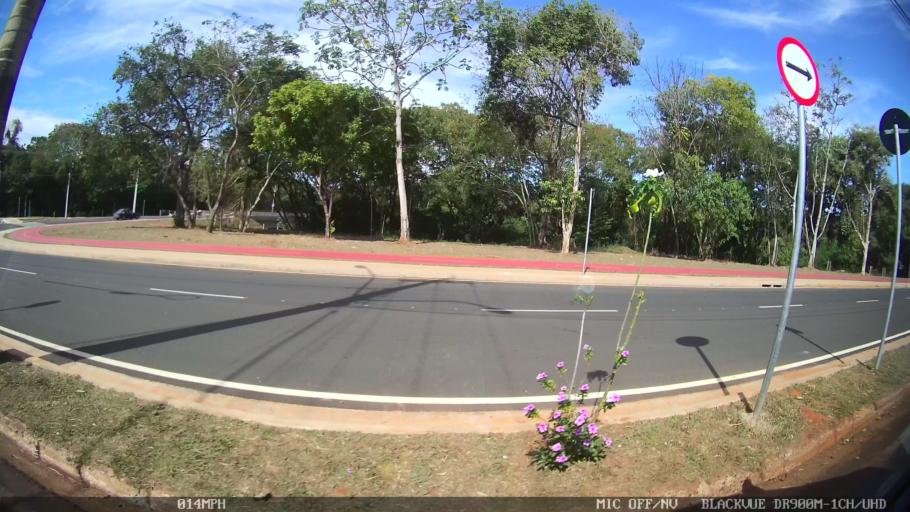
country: BR
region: Sao Paulo
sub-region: Sao Jose Do Rio Preto
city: Sao Jose do Rio Preto
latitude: -20.8380
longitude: -49.3460
